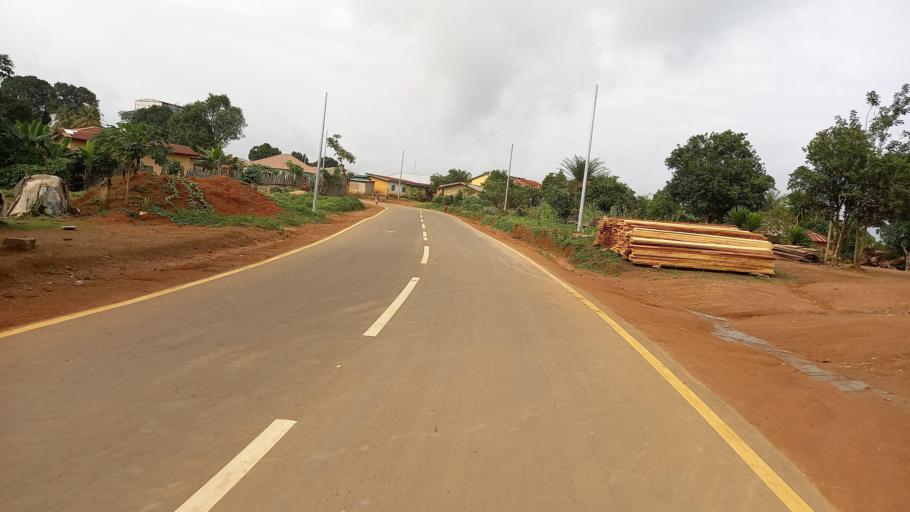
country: SL
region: Eastern Province
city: Kailahun
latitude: 8.2702
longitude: -10.5795
